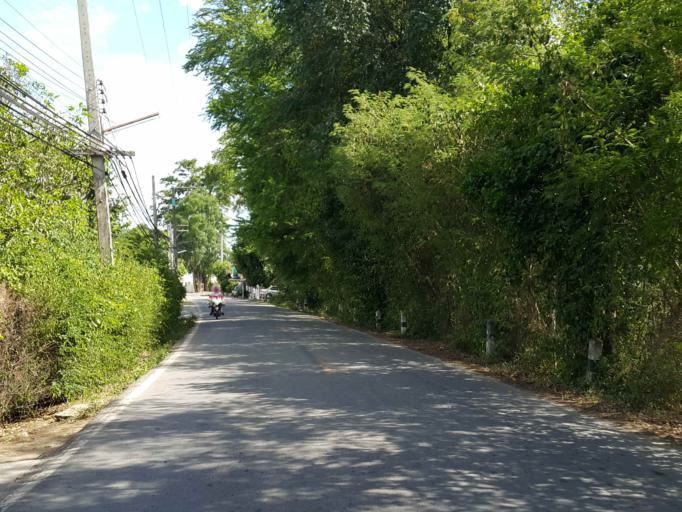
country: TH
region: Chiang Mai
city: Saraphi
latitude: 18.7308
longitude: 98.9980
